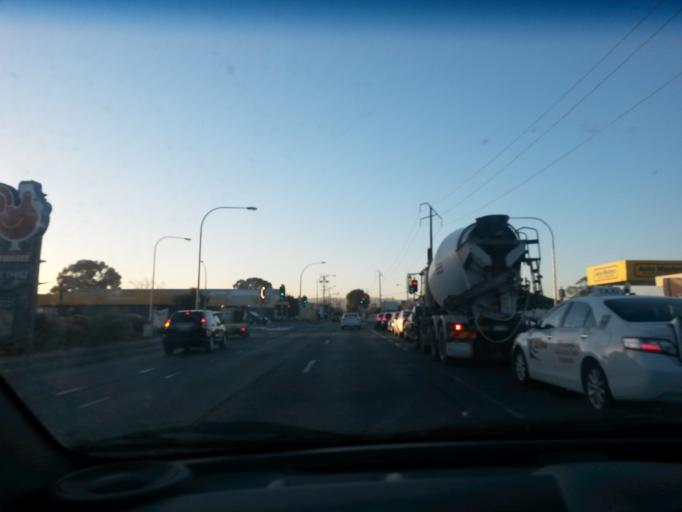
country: AU
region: South Australia
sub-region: Charles Sturt
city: Woodville
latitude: -34.8763
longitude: 138.5502
